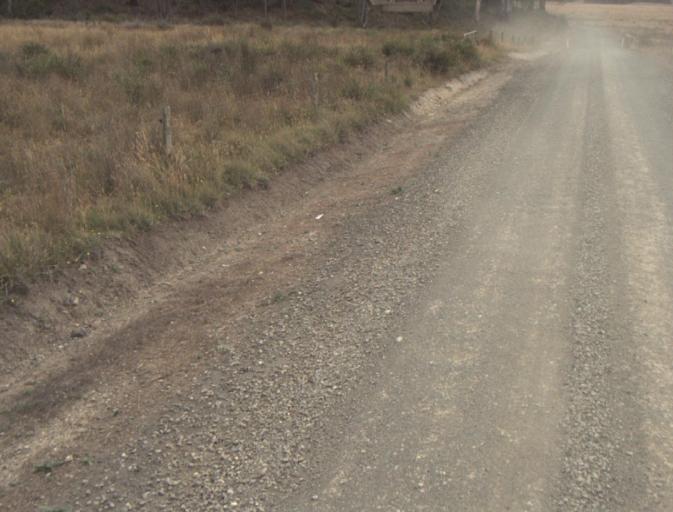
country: AU
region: Tasmania
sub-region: Northern Midlands
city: Evandale
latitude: -41.4745
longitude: 147.4457
